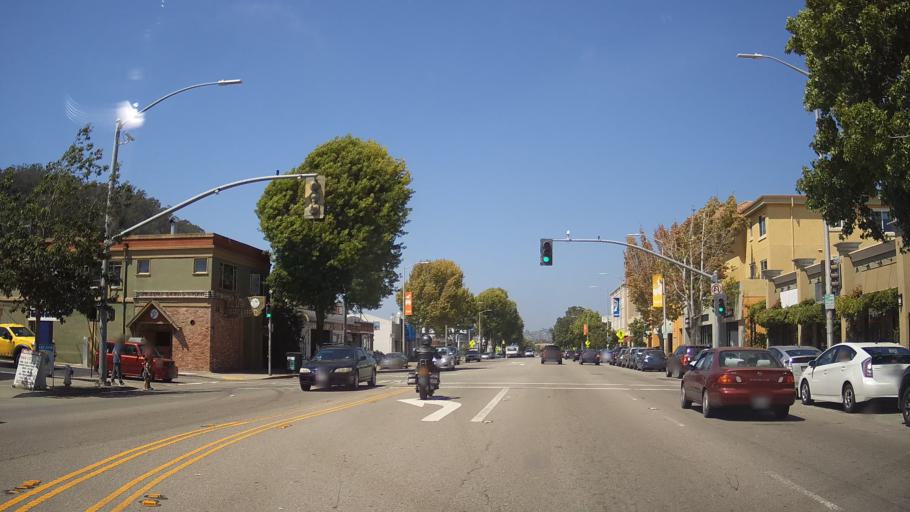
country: US
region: California
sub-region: Alameda County
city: Albany
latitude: 37.8918
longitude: -122.2994
